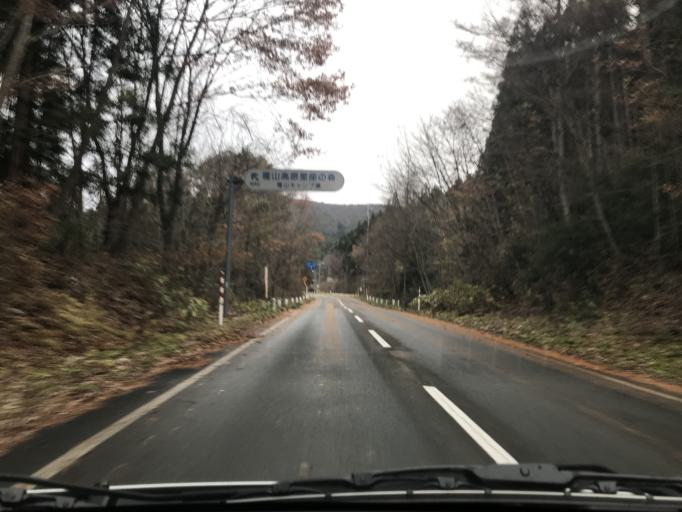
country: JP
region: Iwate
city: Tono
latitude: 39.1760
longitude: 141.3682
